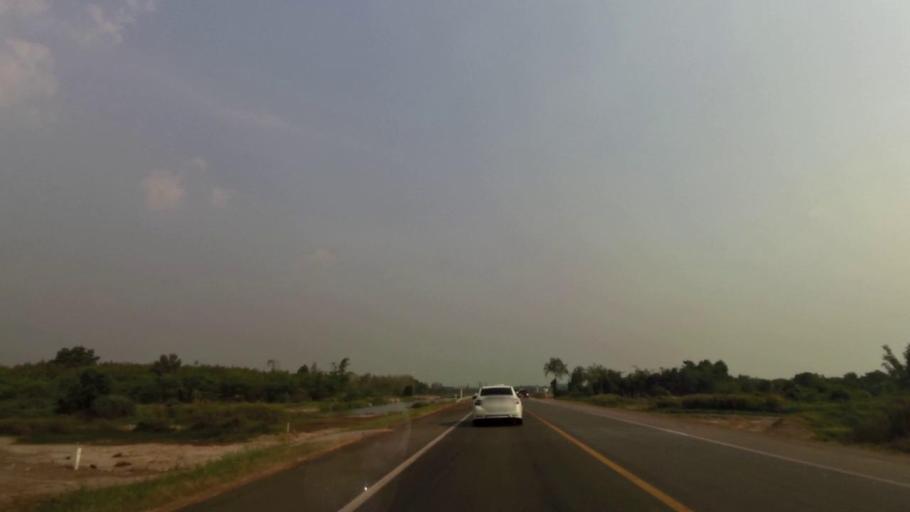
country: TH
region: Rayong
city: Klaeng
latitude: 12.7955
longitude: 101.6704
